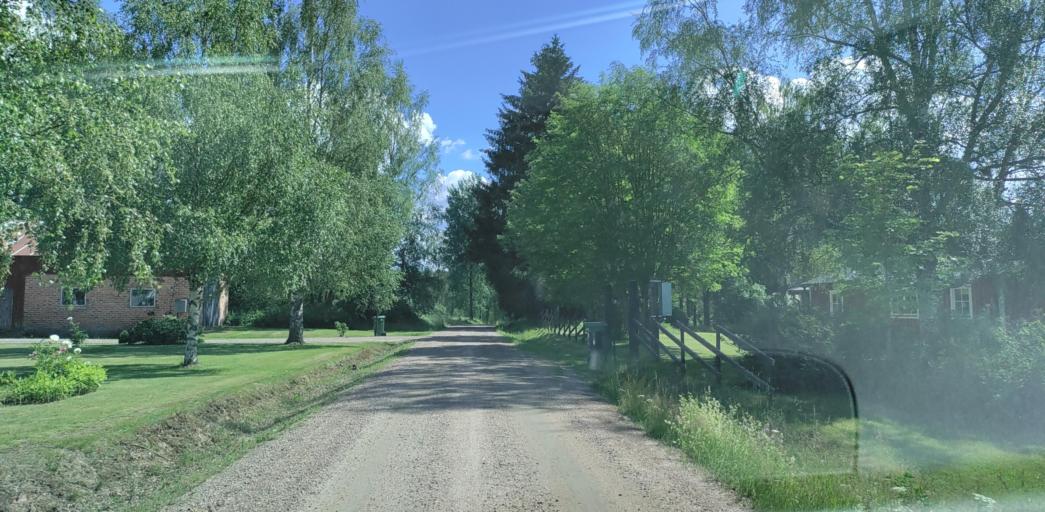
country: SE
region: Vaermland
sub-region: Munkfors Kommun
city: Munkfors
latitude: 59.9511
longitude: 13.4945
